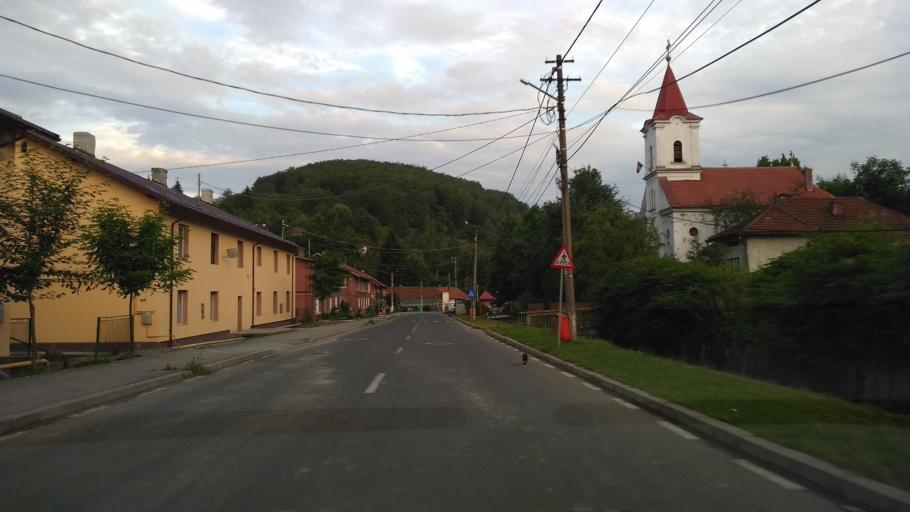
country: RO
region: Hunedoara
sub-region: Comuna Aninoasa
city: Aninoasa
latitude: 45.4056
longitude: 23.3197
